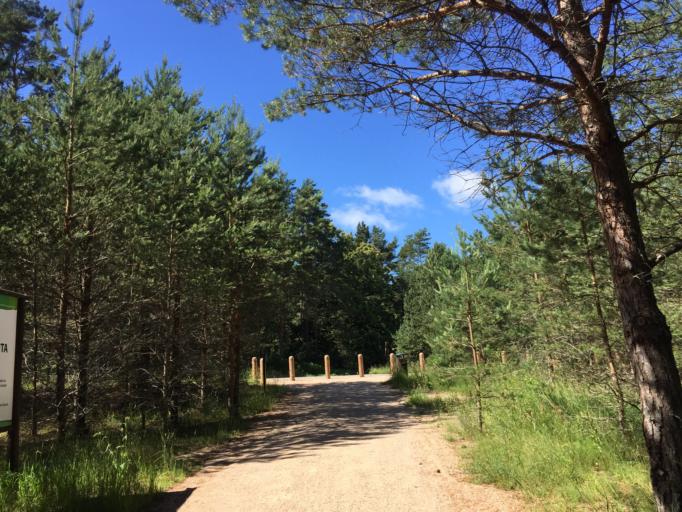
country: LV
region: Ventspils
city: Ventspils
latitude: 57.4523
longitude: 21.6289
